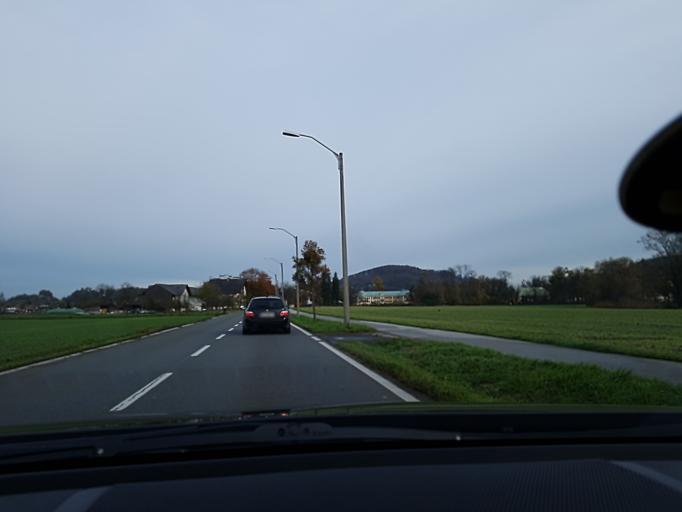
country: AT
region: Salzburg
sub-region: Politischer Bezirk Salzburg-Umgebung
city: Anif
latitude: 47.7749
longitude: 13.0581
